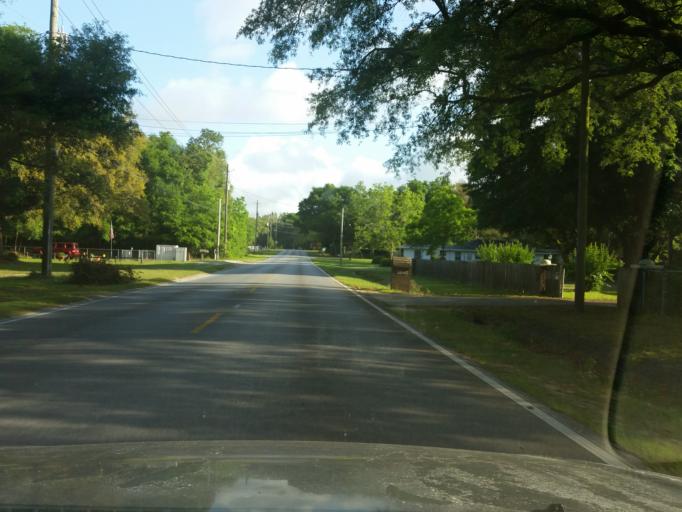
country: US
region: Florida
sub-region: Escambia County
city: Bellview
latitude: 30.4462
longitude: -87.3113
